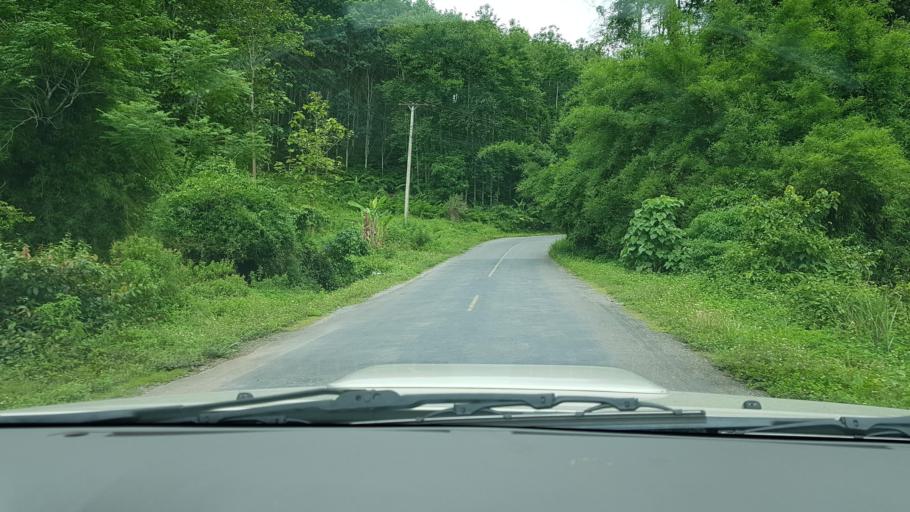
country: LA
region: Loungnamtha
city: Muang Nale
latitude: 20.3865
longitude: 101.7452
